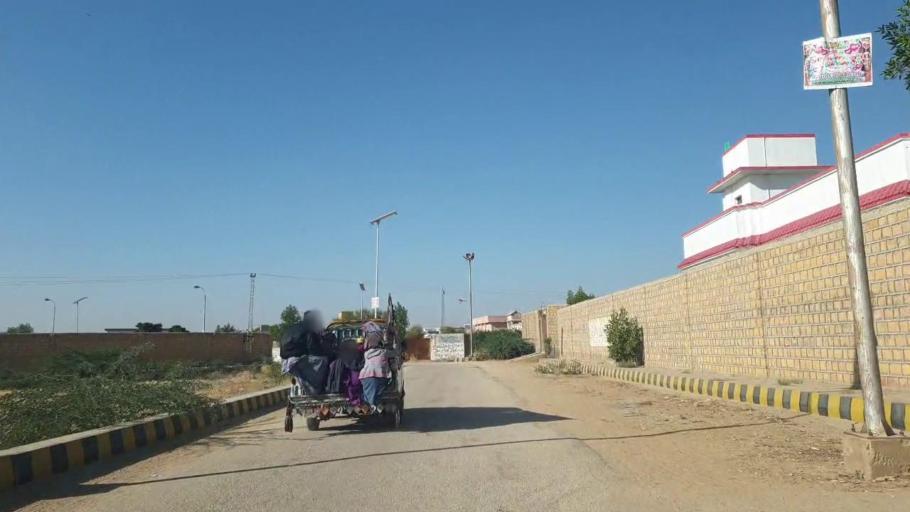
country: PK
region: Sindh
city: Malir Cantonment
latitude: 25.2903
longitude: 67.5762
